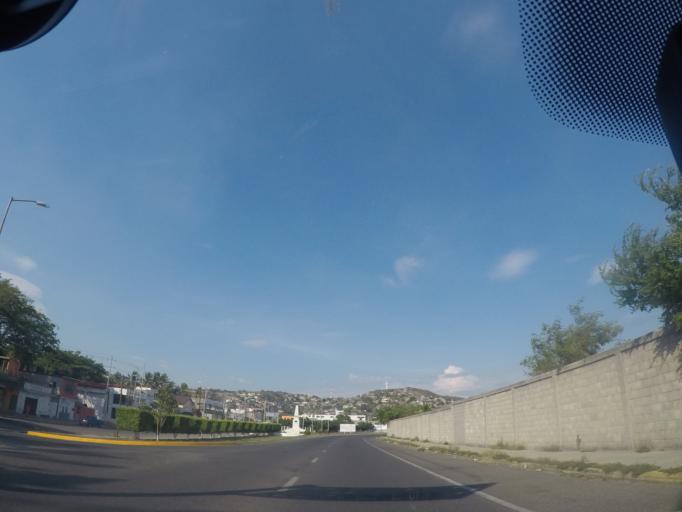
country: MX
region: Oaxaca
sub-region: Salina Cruz
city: Salina Cruz
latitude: 16.1742
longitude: -95.1960
